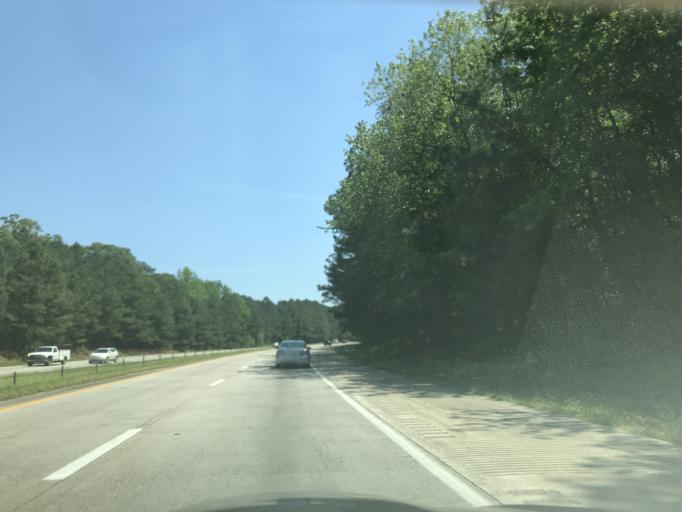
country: US
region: North Carolina
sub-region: Johnston County
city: Benson
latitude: 35.4542
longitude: -78.5352
